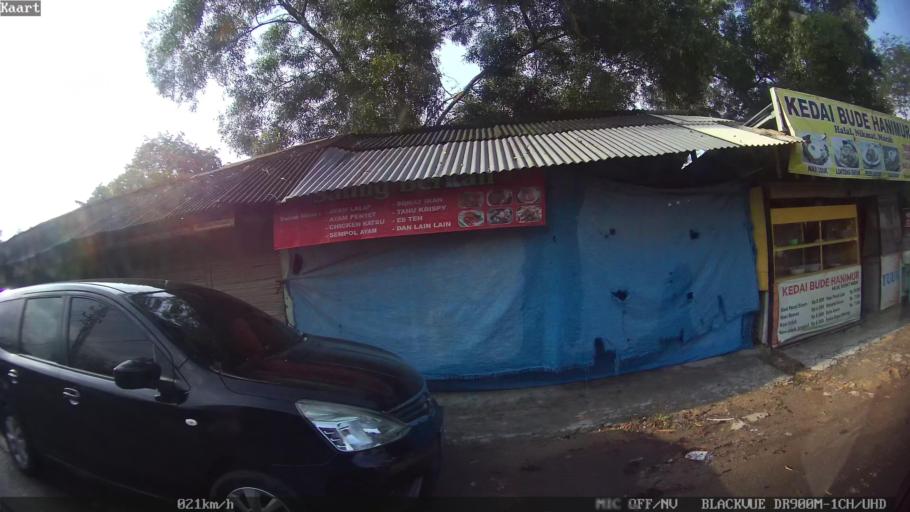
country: ID
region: Lampung
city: Kedaton
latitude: -5.3857
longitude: 105.3087
